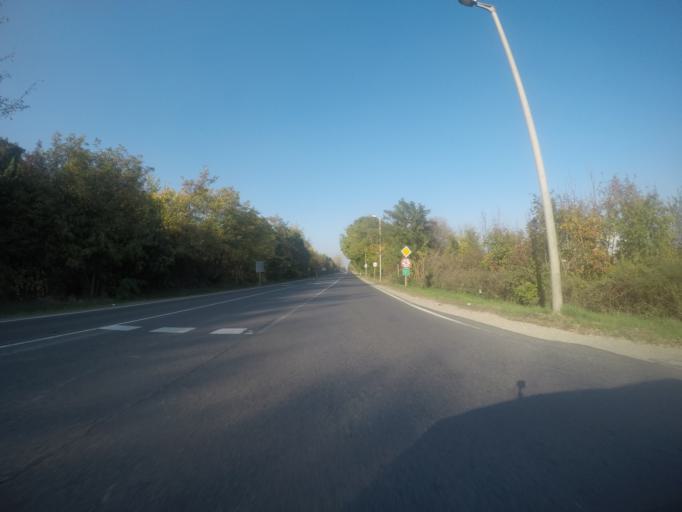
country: HU
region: Pest
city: Szazhalombatta
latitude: 47.3176
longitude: 18.8904
